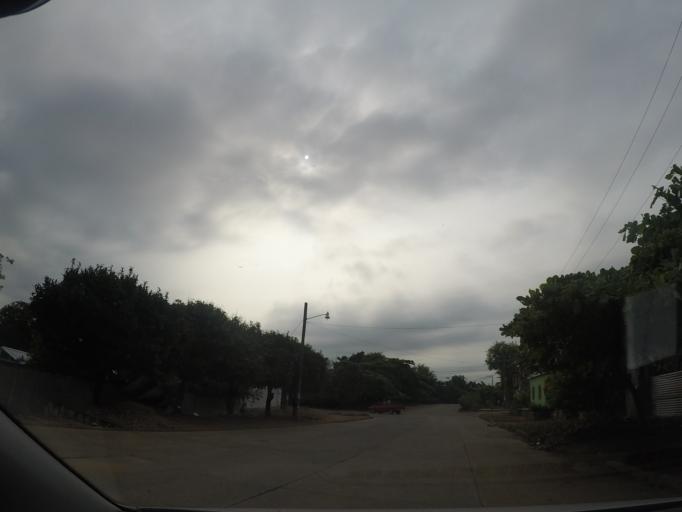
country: MX
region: Oaxaca
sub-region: Santa Maria Petapa
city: Llano Suchiapa
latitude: 16.8689
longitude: -95.0479
